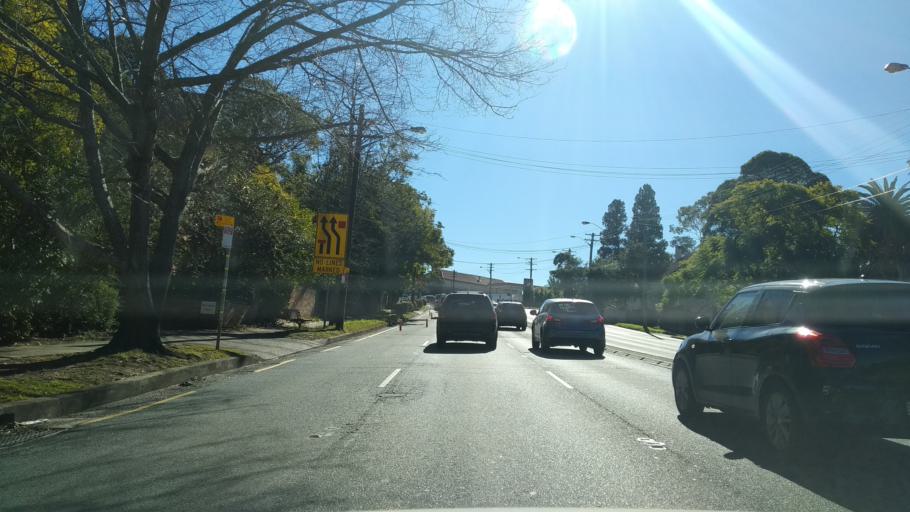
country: AU
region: New South Wales
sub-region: City of Sydney
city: Pymble
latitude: -33.7346
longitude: 151.1320
